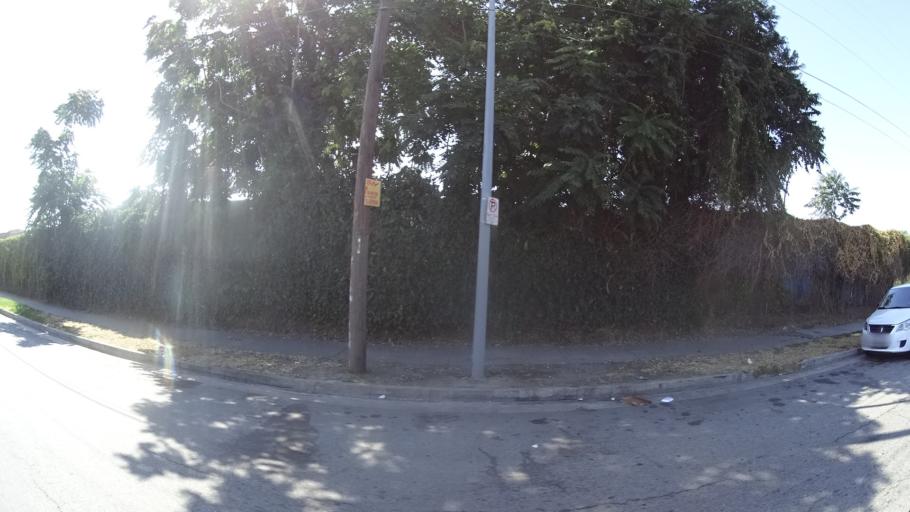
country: US
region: California
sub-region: Los Angeles County
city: View Park-Windsor Hills
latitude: 33.9841
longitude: -118.3185
